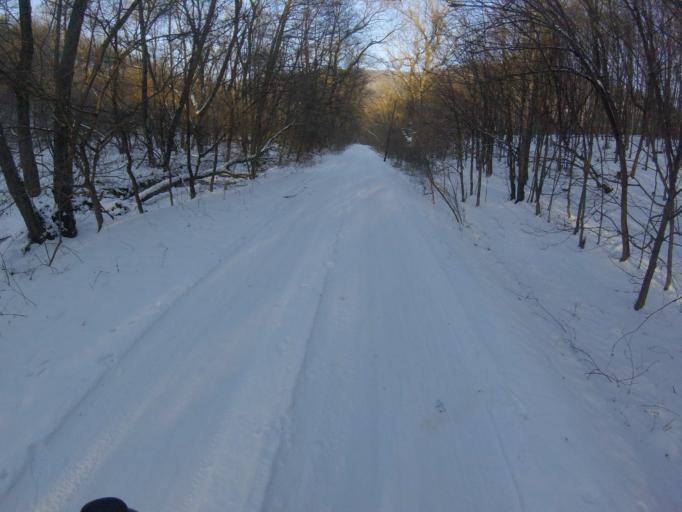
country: SK
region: Nitriansky
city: Sahy
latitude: 47.9961
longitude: 18.9011
